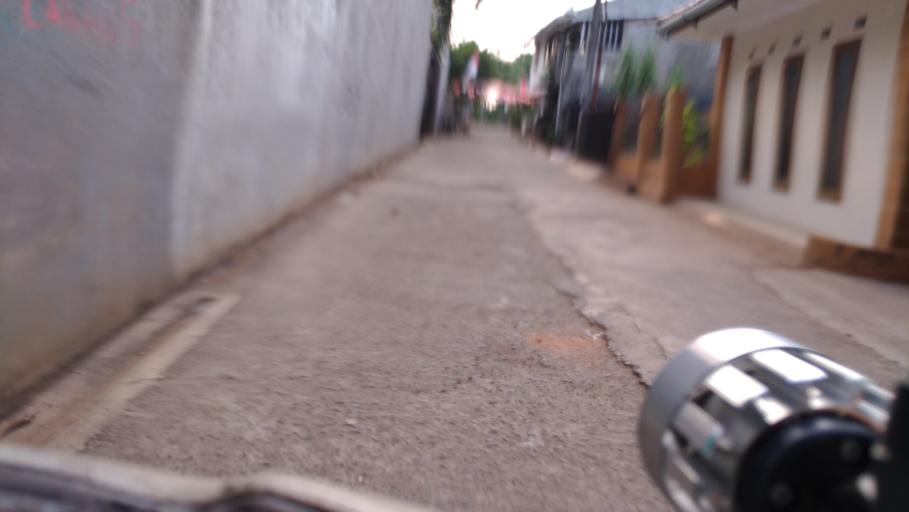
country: ID
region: West Java
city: Cileungsir
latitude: -6.3675
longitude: 106.9041
